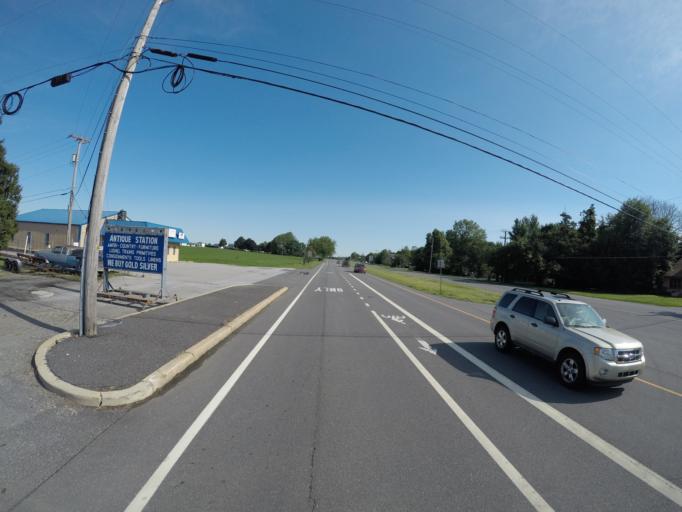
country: US
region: Delaware
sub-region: New Castle County
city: Delaware City
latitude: 39.5604
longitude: -75.6534
